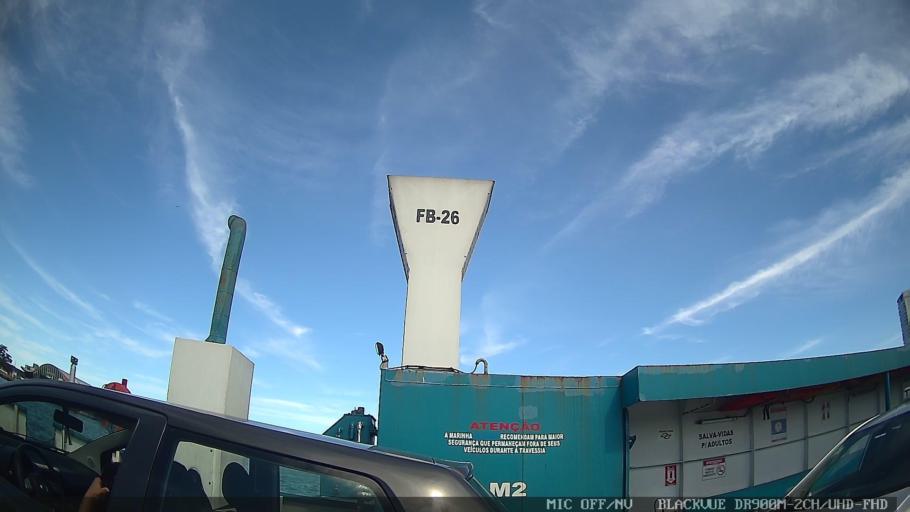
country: BR
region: Sao Paulo
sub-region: Guaruja
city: Guaruja
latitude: -23.9871
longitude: -46.2916
